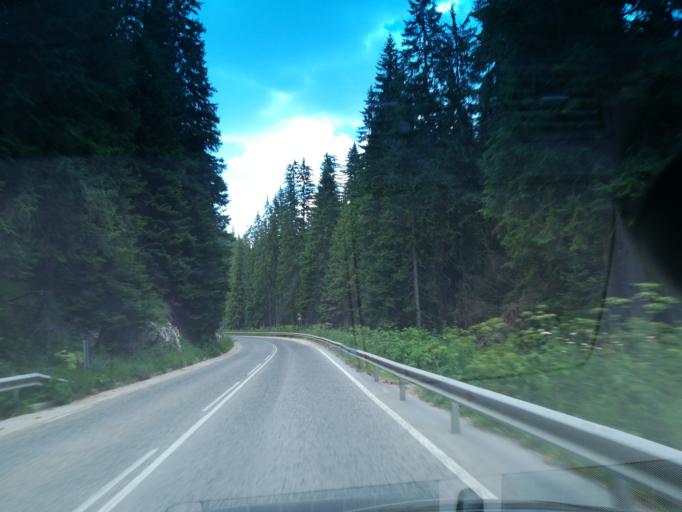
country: BG
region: Smolyan
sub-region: Obshtina Chepelare
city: Chepelare
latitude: 41.6610
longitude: 24.7134
